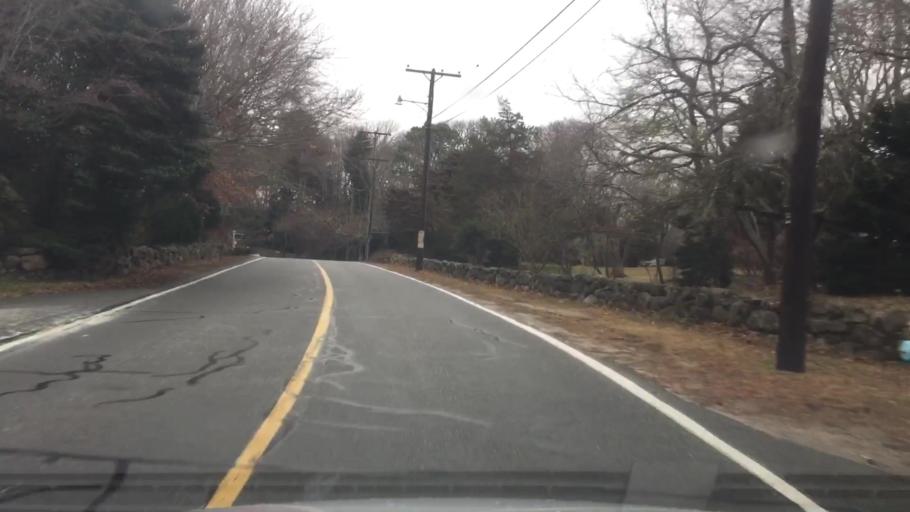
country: US
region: Massachusetts
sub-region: Barnstable County
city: Falmouth
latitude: 41.5197
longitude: -70.6616
